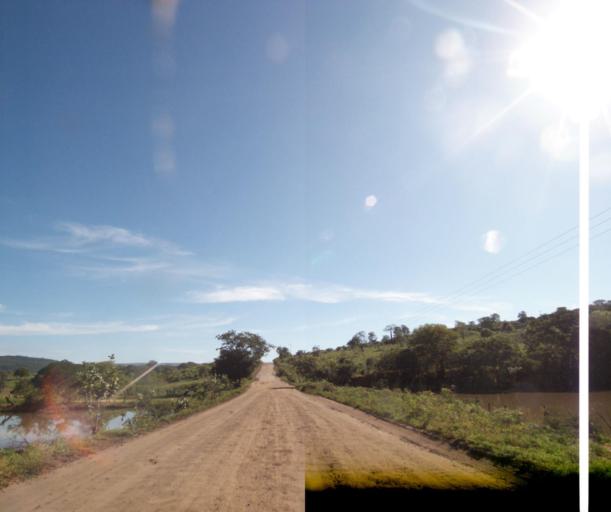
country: BR
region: Bahia
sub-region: Sao Felix Do Coribe
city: Santa Maria da Vitoria
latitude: -13.6374
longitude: -44.4351
